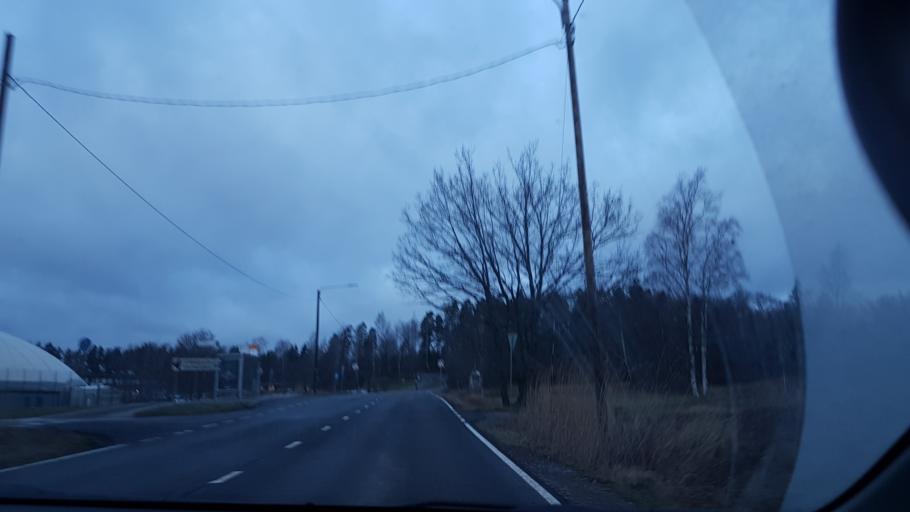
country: FI
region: Uusimaa
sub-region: Helsinki
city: Vantaa
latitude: 60.2790
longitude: 25.1258
